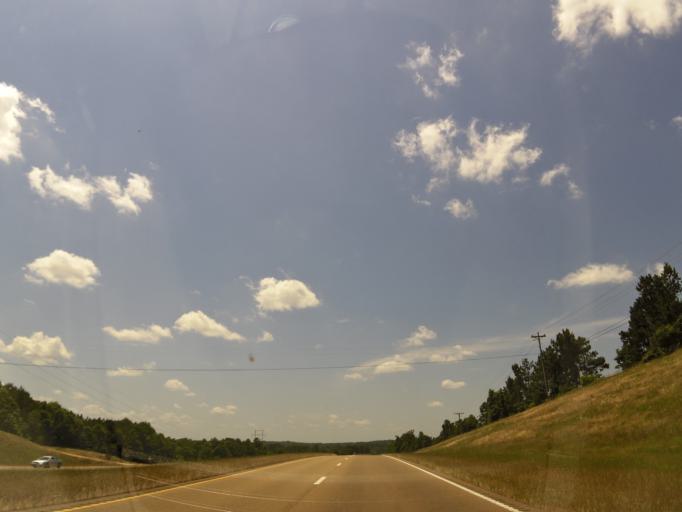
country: US
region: Mississippi
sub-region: Lafayette County
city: Oxford
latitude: 34.3229
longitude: -89.3811
